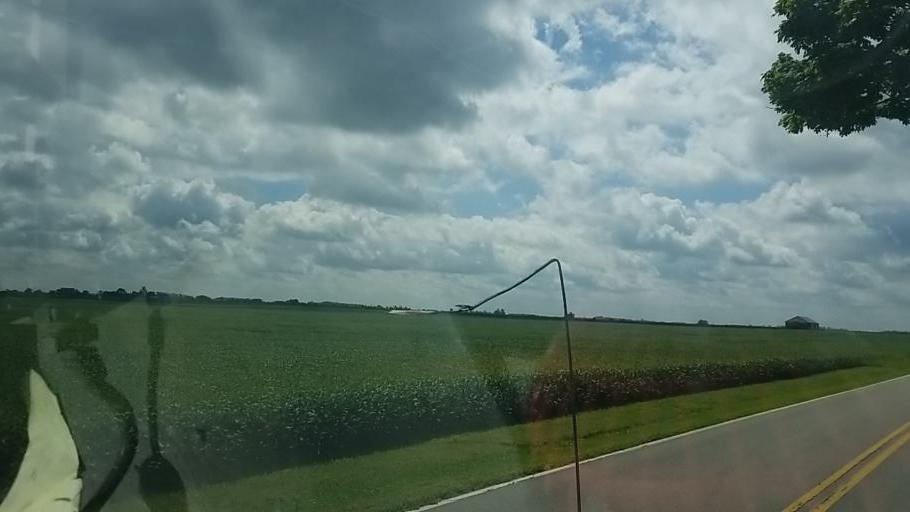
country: US
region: Ohio
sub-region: Fayette County
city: Jeffersonville
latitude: 39.6853
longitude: -83.5036
